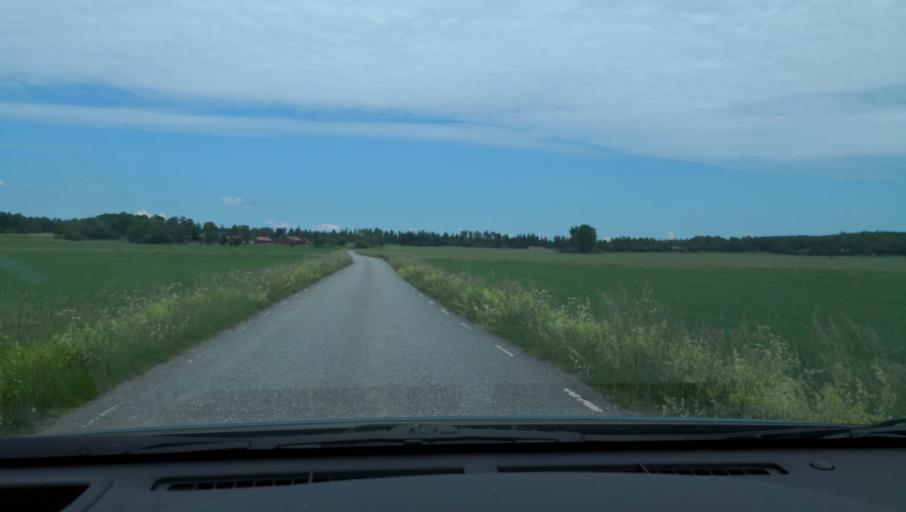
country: SE
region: Uppsala
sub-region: Enkopings Kommun
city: Orsundsbro
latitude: 59.6983
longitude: 17.4095
